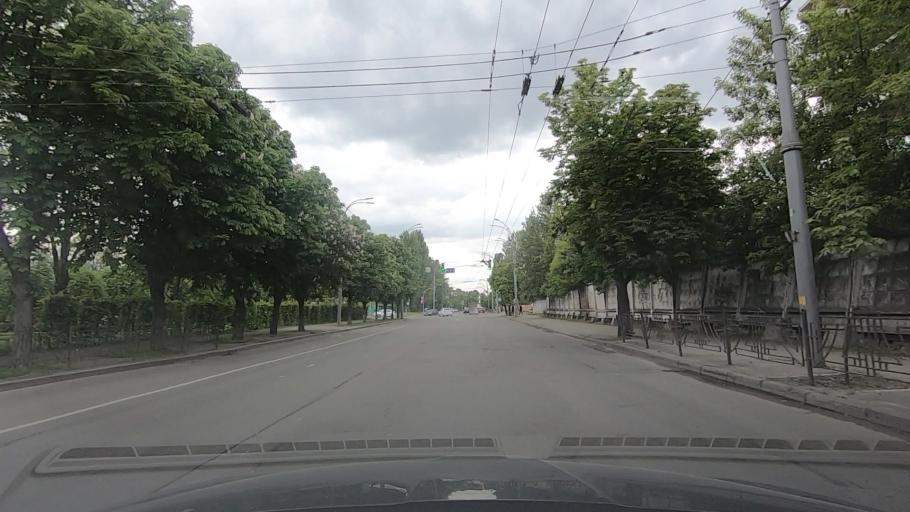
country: MD
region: Riscani
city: Riscani
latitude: 48.0517
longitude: 27.5894
